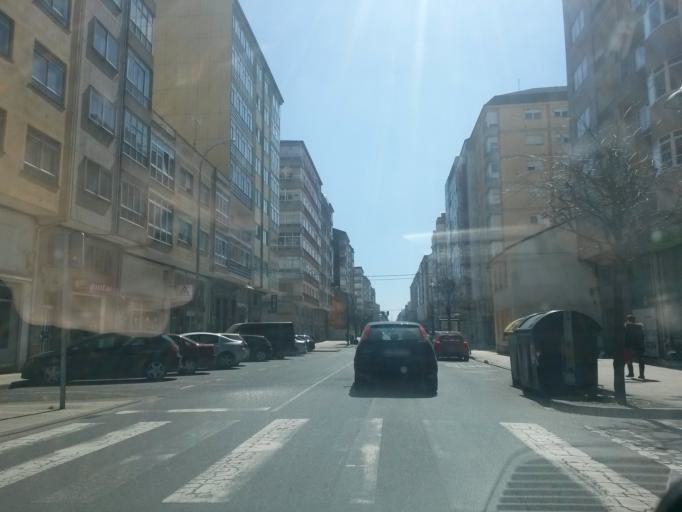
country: ES
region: Galicia
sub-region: Provincia de Lugo
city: Lugo
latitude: 43.0254
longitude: -7.5671
